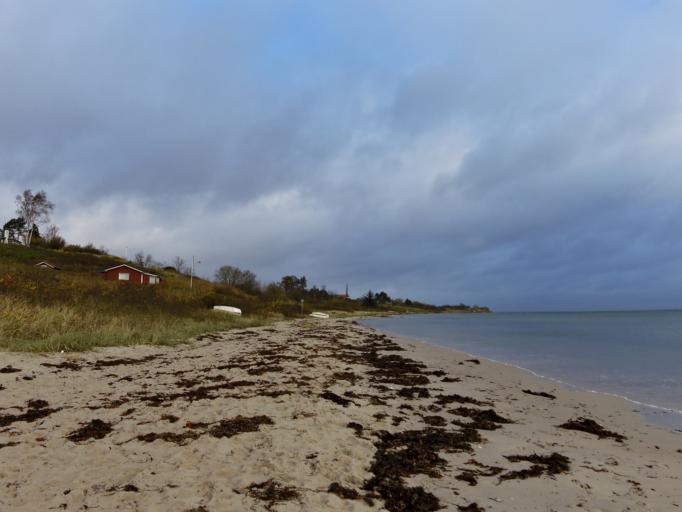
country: DK
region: Central Jutland
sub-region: Arhus Kommune
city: Malling
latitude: 55.9926
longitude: 10.2535
